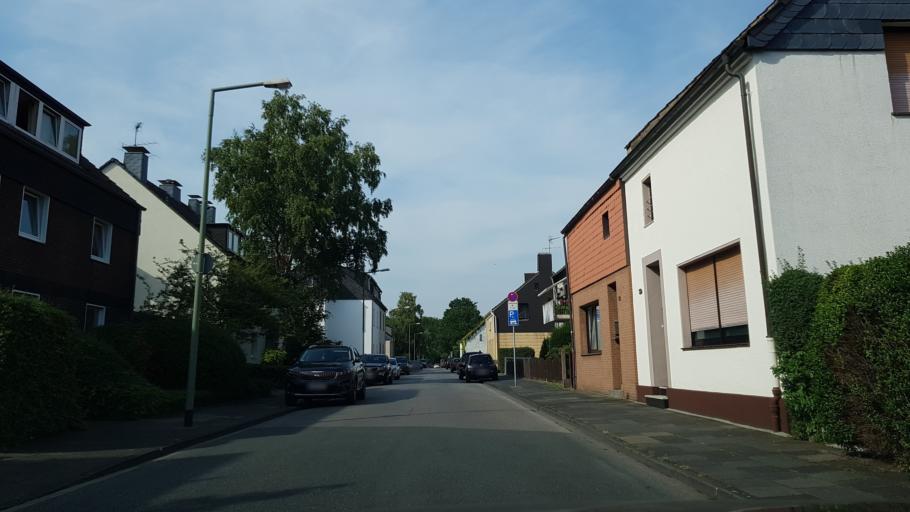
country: DE
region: North Rhine-Westphalia
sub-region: Regierungsbezirk Dusseldorf
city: Hochfeld
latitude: 51.3871
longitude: 6.7676
